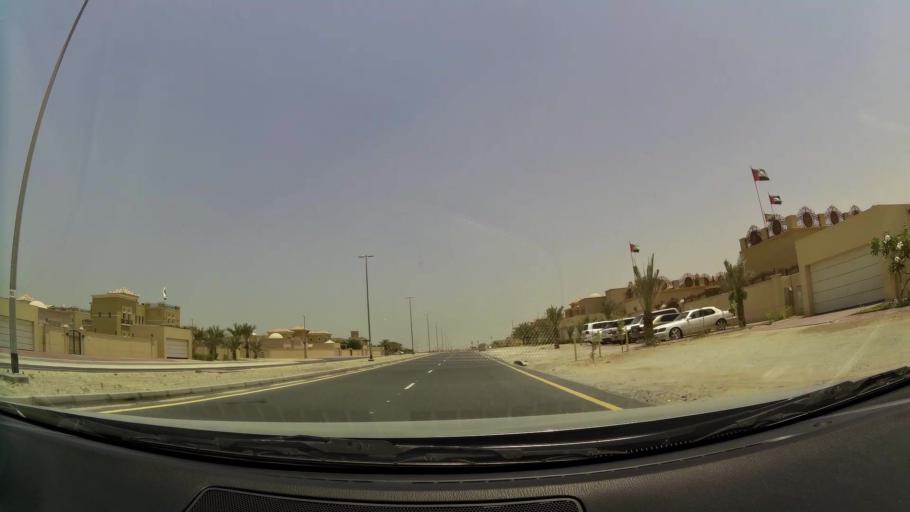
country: AE
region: Dubai
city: Dubai
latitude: 25.0822
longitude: 55.2406
